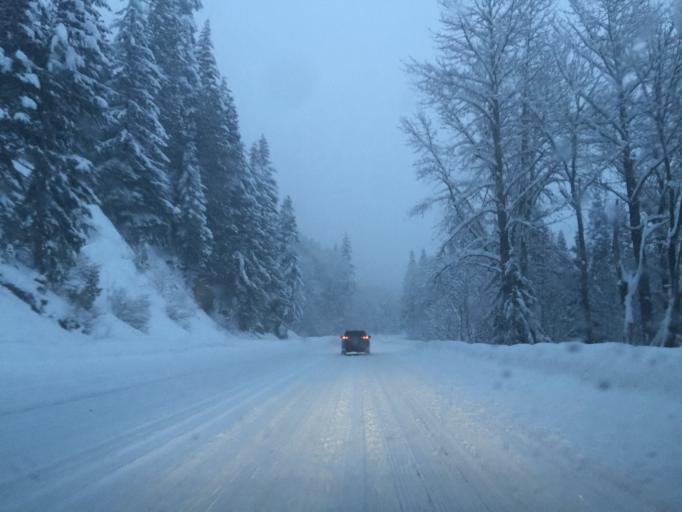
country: US
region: Washington
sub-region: Chelan County
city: Leavenworth
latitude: 47.7907
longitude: -120.8669
